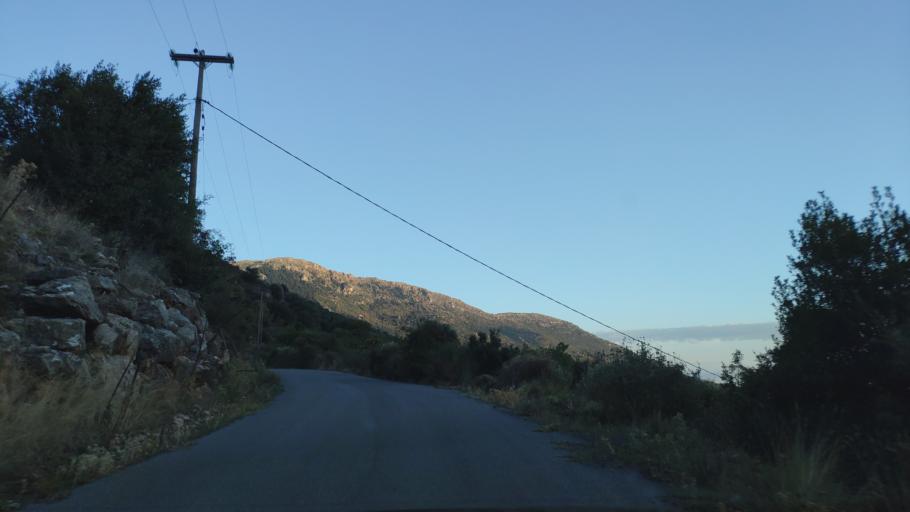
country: GR
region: Peloponnese
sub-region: Nomos Arkadias
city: Dimitsana
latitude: 37.5874
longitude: 22.0418
